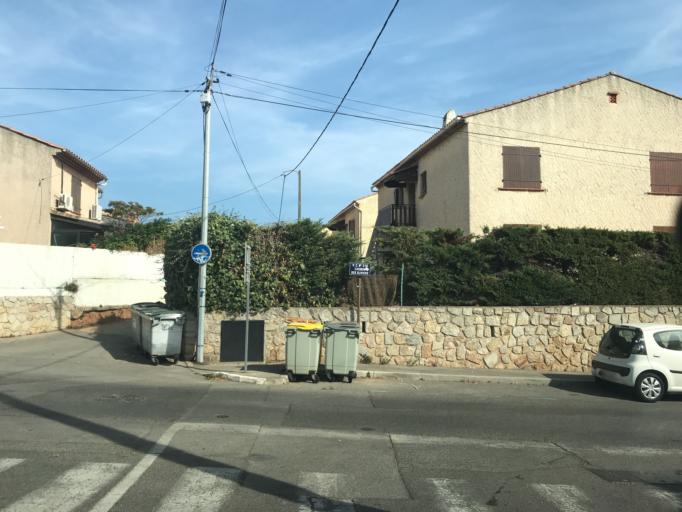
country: FR
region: Provence-Alpes-Cote d'Azur
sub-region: Departement du Var
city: La Seyne-sur-Mer
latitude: 43.0836
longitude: 5.8793
